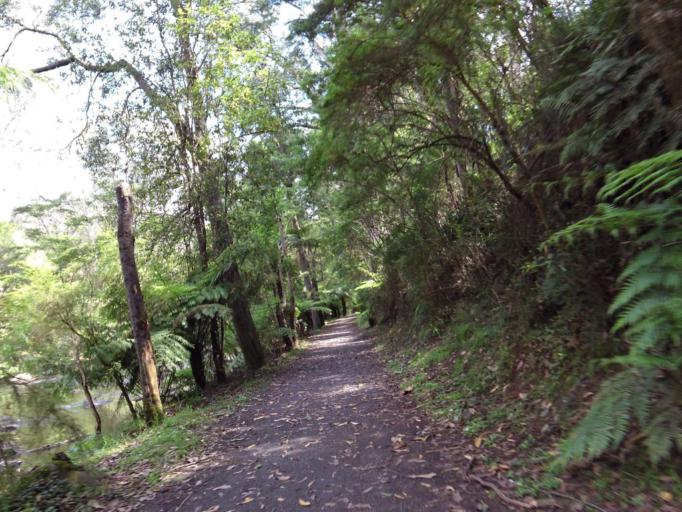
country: AU
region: Victoria
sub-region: Yarra Ranges
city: Millgrove
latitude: -37.7475
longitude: 145.7150
